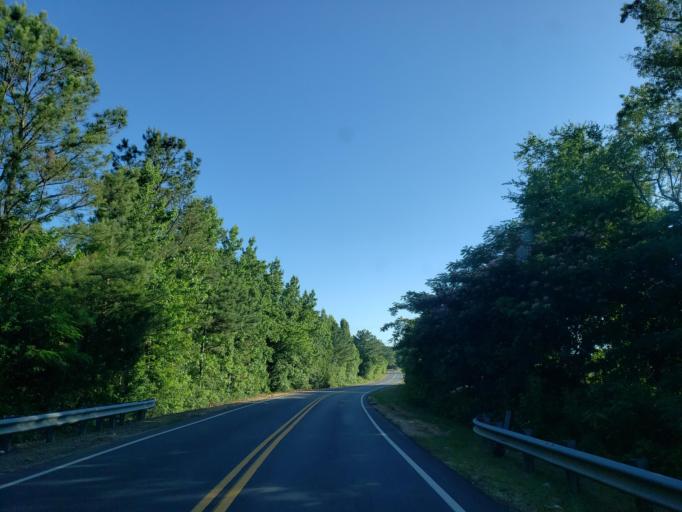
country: US
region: Georgia
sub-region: Floyd County
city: Shannon
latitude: 34.3605
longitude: -85.1405
